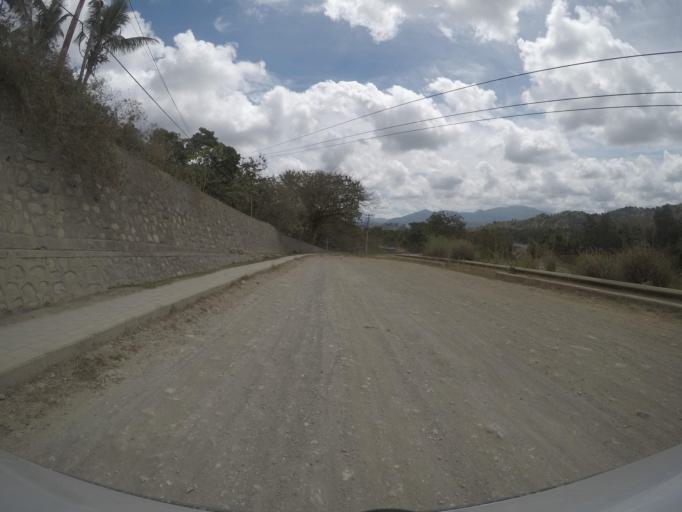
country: TL
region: Viqueque
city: Viqueque
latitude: -8.8648
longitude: 126.3618
